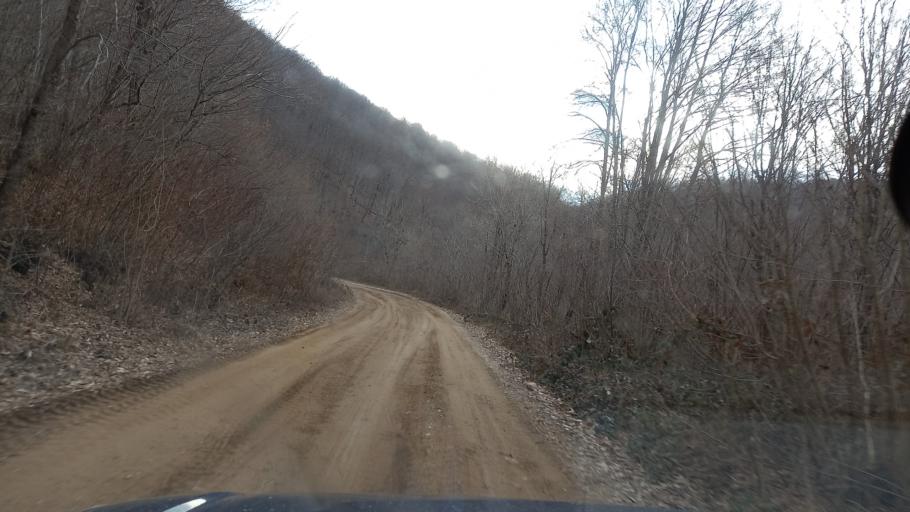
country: RU
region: Adygeya
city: Kamennomostskiy
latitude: 44.1662
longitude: 40.2997
